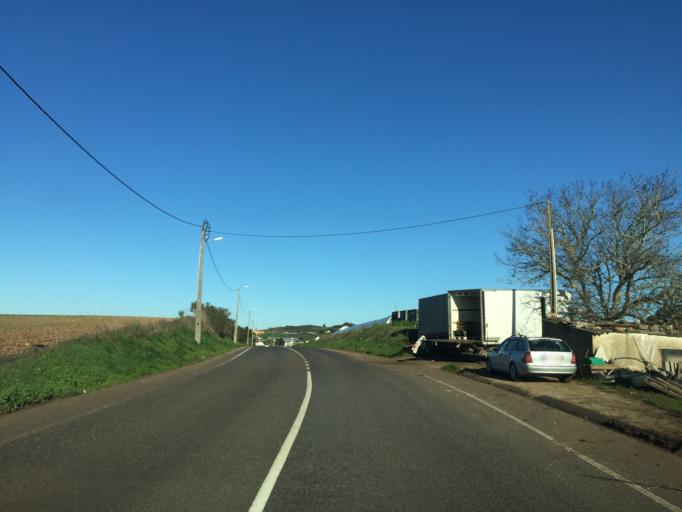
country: PT
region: Lisbon
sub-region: Sintra
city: Almargem
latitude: 38.8593
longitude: -9.2776
